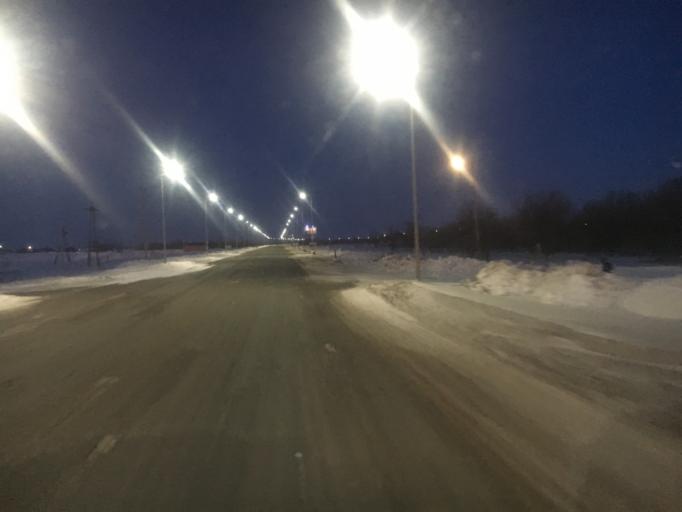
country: KZ
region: Batys Qazaqstan
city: Oral
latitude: 51.1585
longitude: 51.5017
